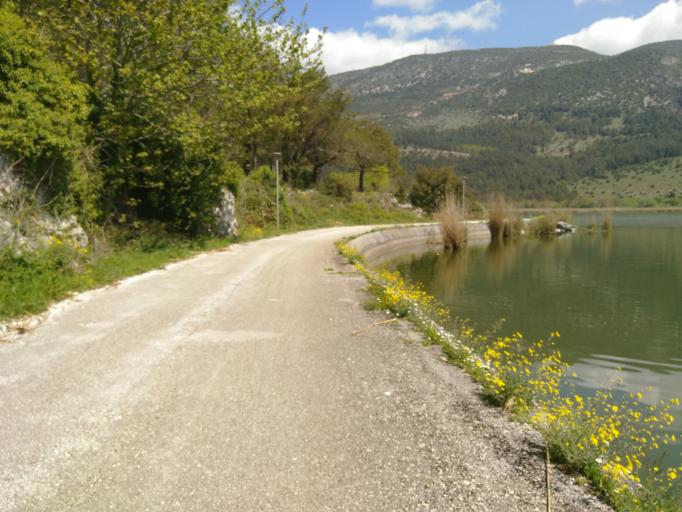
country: GR
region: Epirus
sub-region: Nomos Ioanninon
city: Ioannina
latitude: 39.6755
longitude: 20.8782
